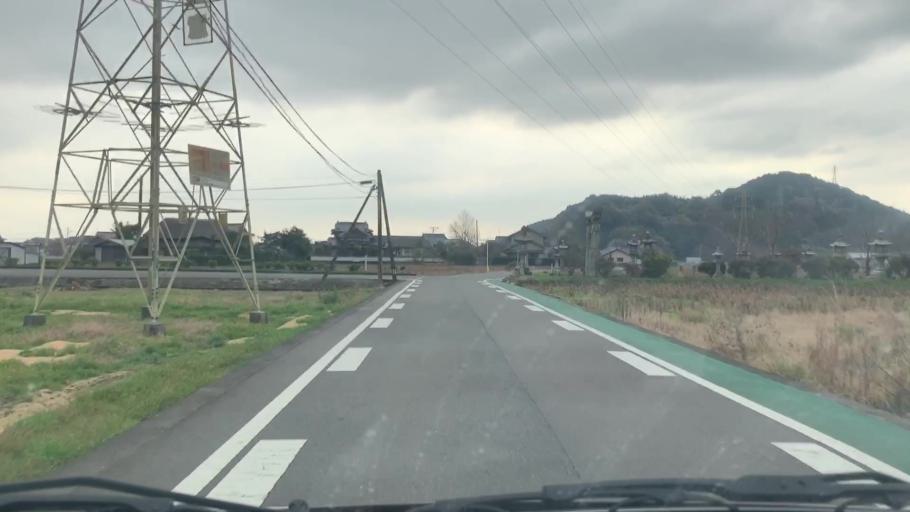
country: JP
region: Saga Prefecture
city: Kashima
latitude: 33.1223
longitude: 130.0590
